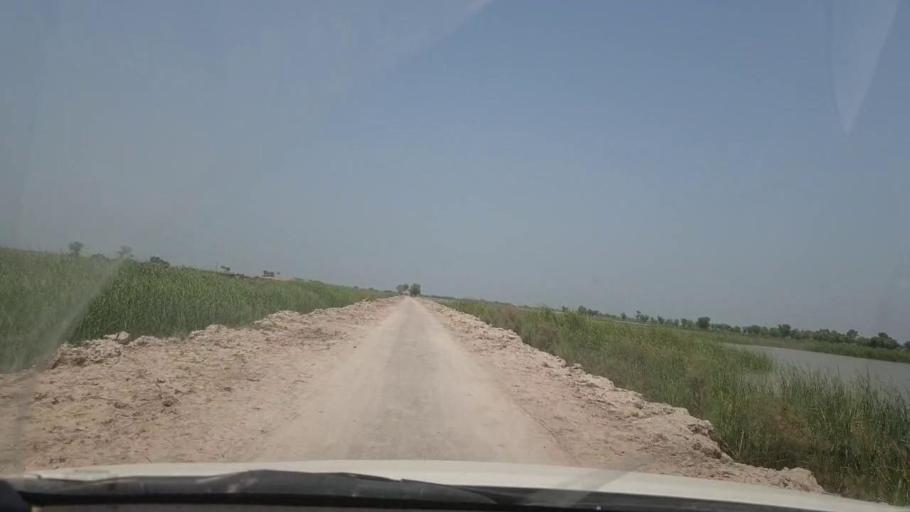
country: PK
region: Sindh
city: Lakhi
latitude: 27.8780
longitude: 68.7348
